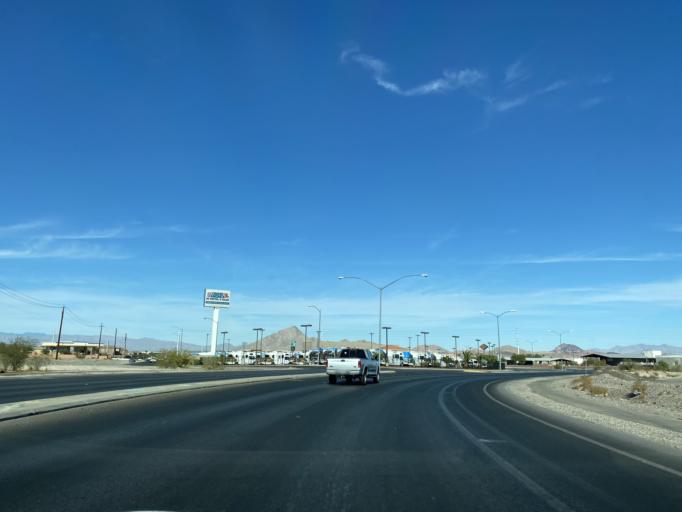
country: US
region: Nevada
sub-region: Clark County
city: Henderson
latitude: 36.0607
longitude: -115.0286
